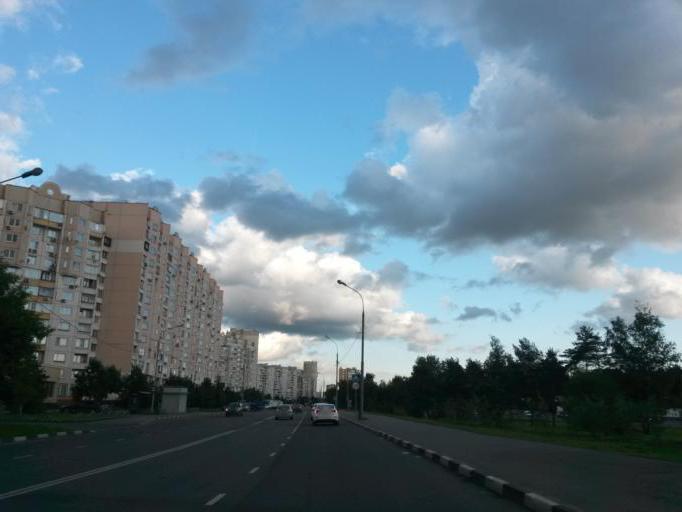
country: RU
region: Moscow
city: Zhulebino
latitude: 55.6831
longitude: 37.8433
